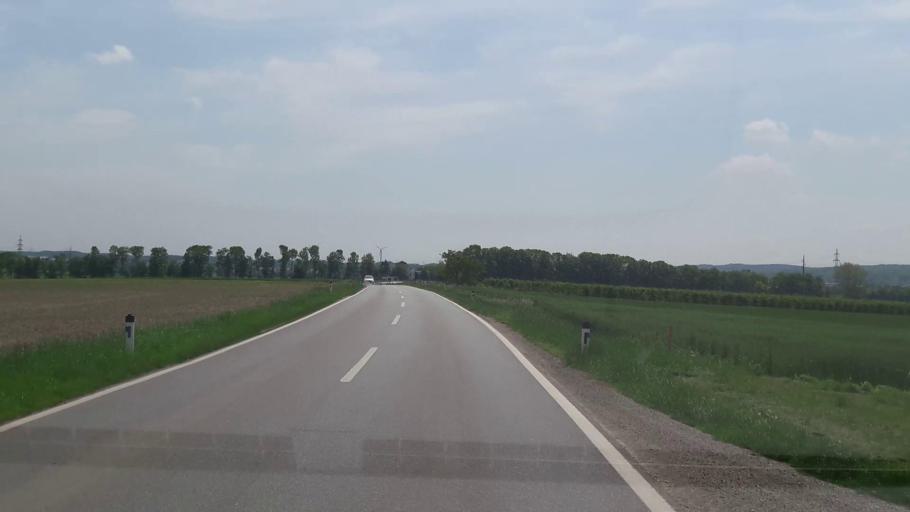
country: AT
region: Lower Austria
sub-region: Politischer Bezirk Bruck an der Leitha
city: Bruck an der Leitha
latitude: 48.0393
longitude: 16.7542
